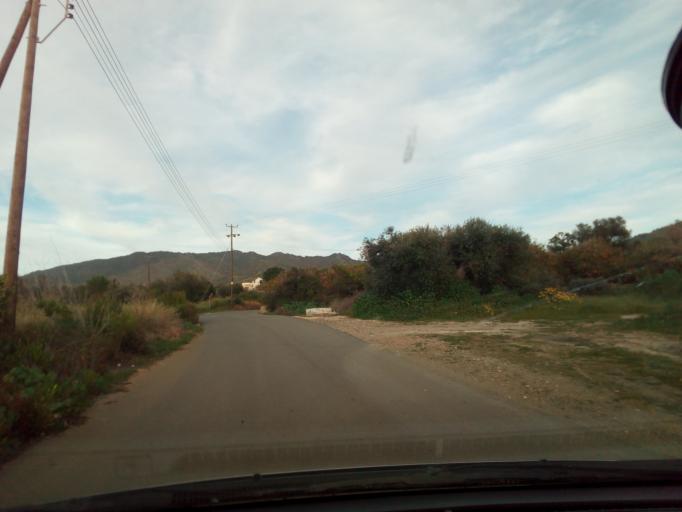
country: CY
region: Pafos
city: Polis
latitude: 35.1148
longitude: 32.5147
